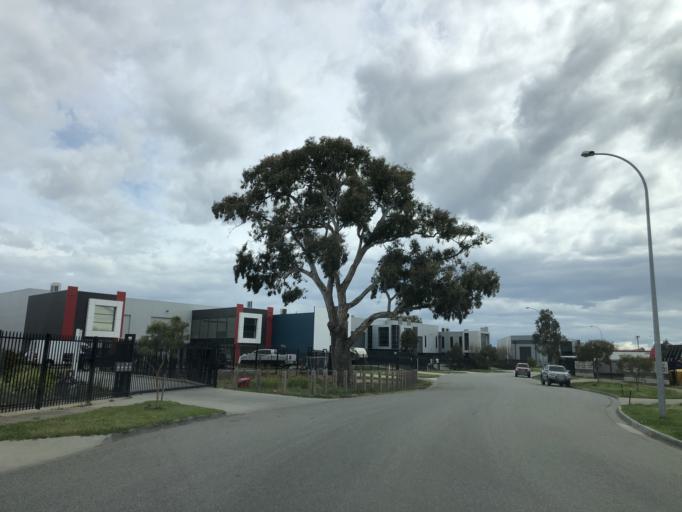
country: AU
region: Victoria
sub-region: Frankston
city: Carrum Downs
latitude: -38.0904
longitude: 145.1698
